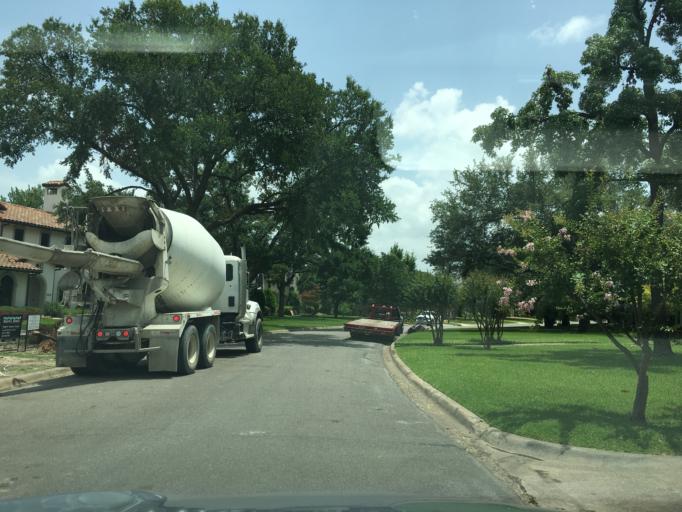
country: US
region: Texas
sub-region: Dallas County
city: University Park
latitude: 32.9070
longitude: -96.8008
